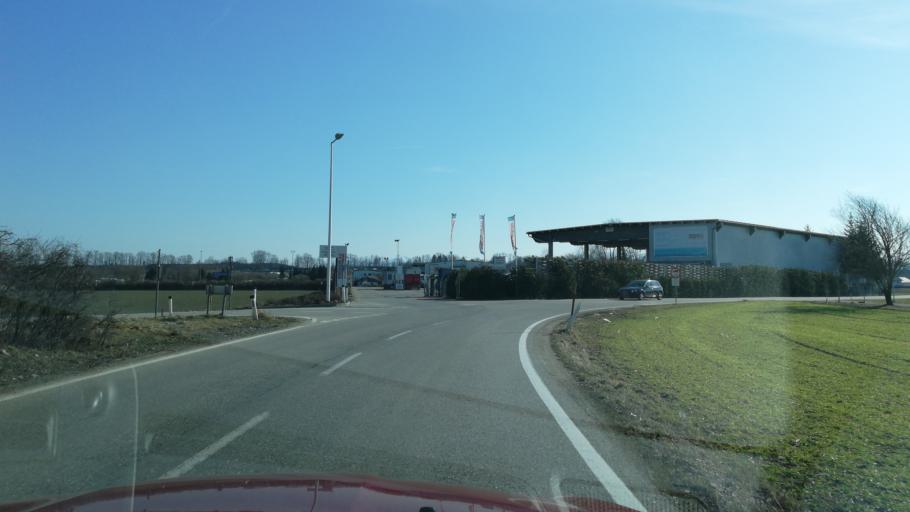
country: AT
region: Upper Austria
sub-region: Politischer Bezirk Vocklabruck
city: Redlham
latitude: 48.0202
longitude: 13.7414
